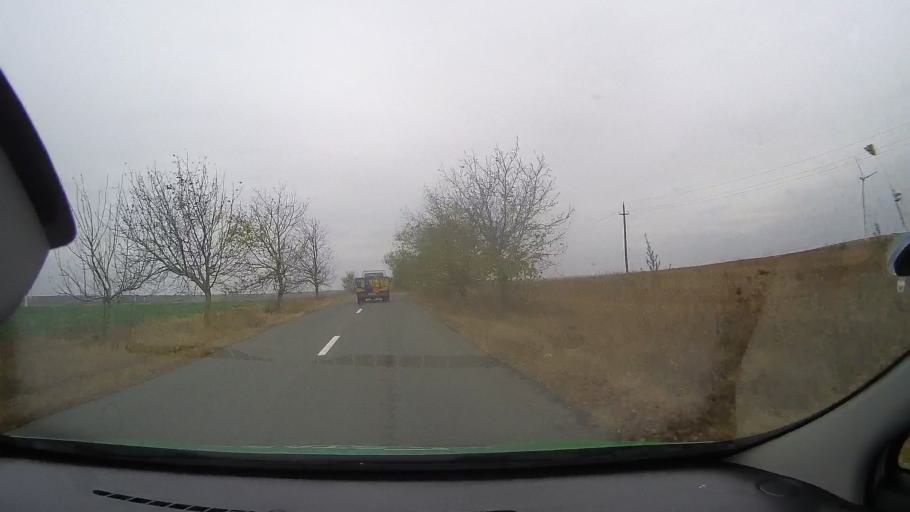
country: RO
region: Constanta
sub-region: Comuna Targusor
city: Targusor
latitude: 44.4804
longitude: 28.3736
